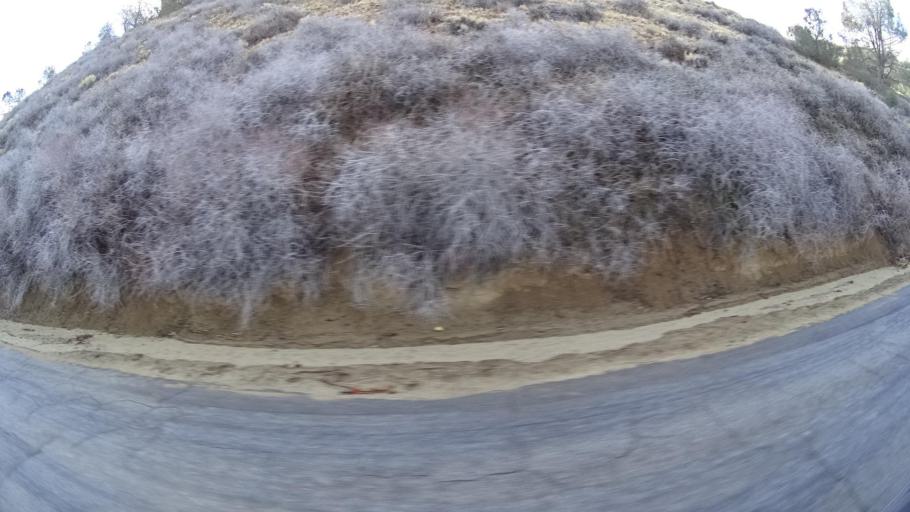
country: US
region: California
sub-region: Kern County
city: Tehachapi
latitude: 35.0801
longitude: -118.3294
